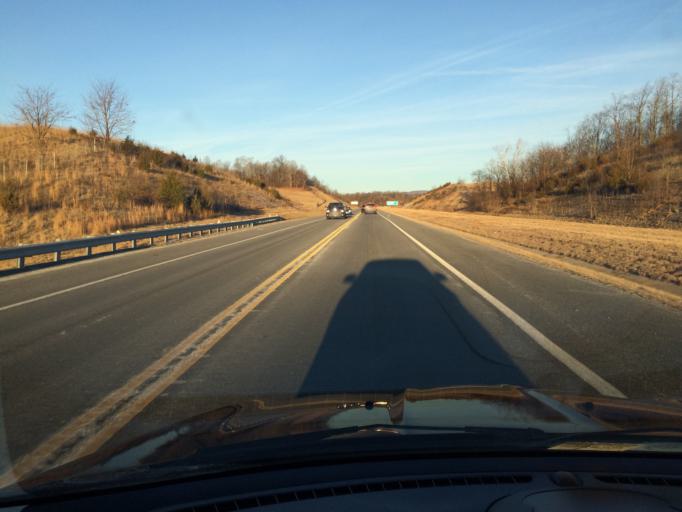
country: US
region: Virginia
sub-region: City of Staunton
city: Staunton
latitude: 38.1367
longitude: -79.1015
